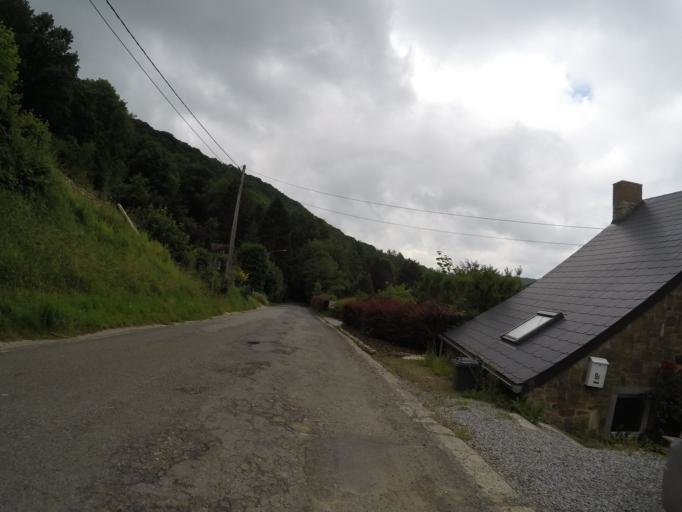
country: BE
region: Wallonia
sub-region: Province de Namur
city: Assesse
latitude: 50.3461
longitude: 4.9532
